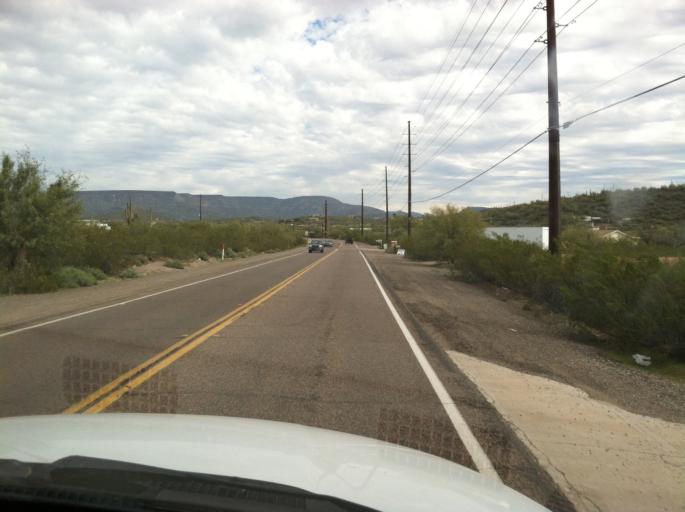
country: US
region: Arizona
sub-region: Maricopa County
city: New River
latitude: 33.9183
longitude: -112.1344
